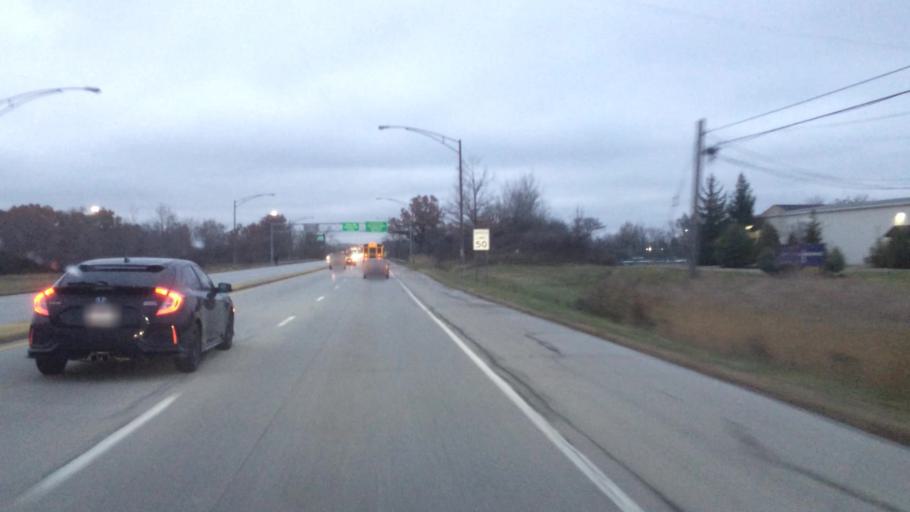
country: US
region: Ohio
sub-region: Cuyahoga County
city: Berea
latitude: 41.3918
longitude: -81.8501
